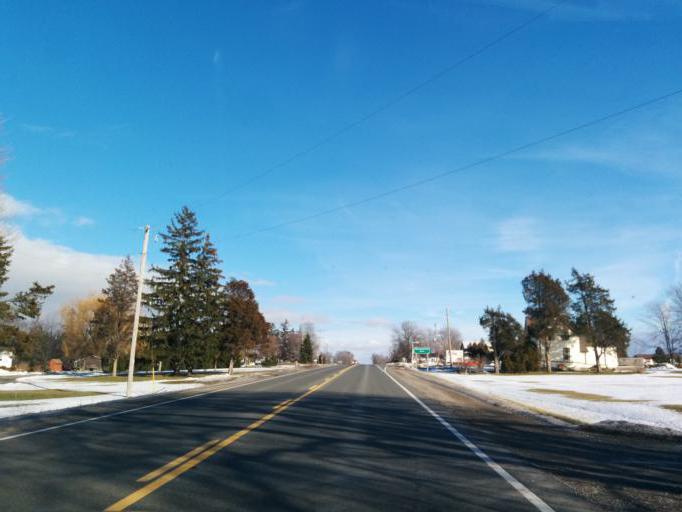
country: CA
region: Ontario
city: Ancaster
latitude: 42.9364
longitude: -79.9141
